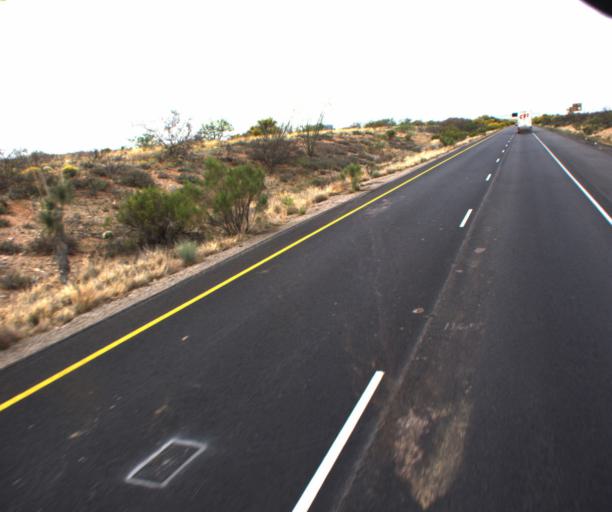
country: US
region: Arizona
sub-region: Pima County
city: Vail
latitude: 32.0004
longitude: -110.6733
